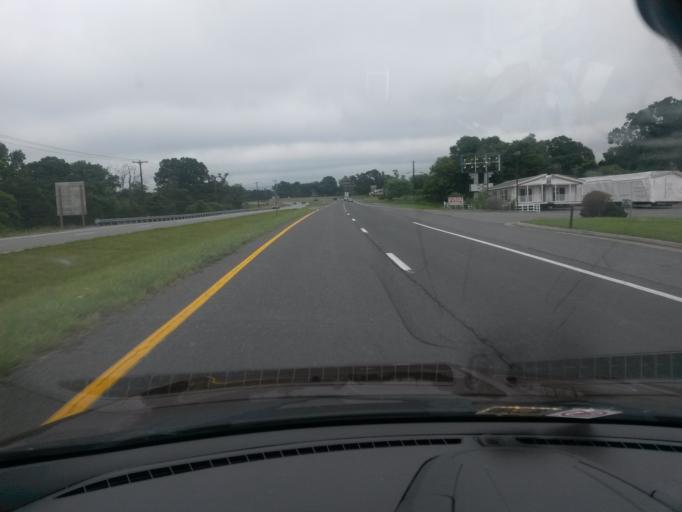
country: US
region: Virginia
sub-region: City of Bedford
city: Bedford
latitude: 37.3221
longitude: -79.4930
